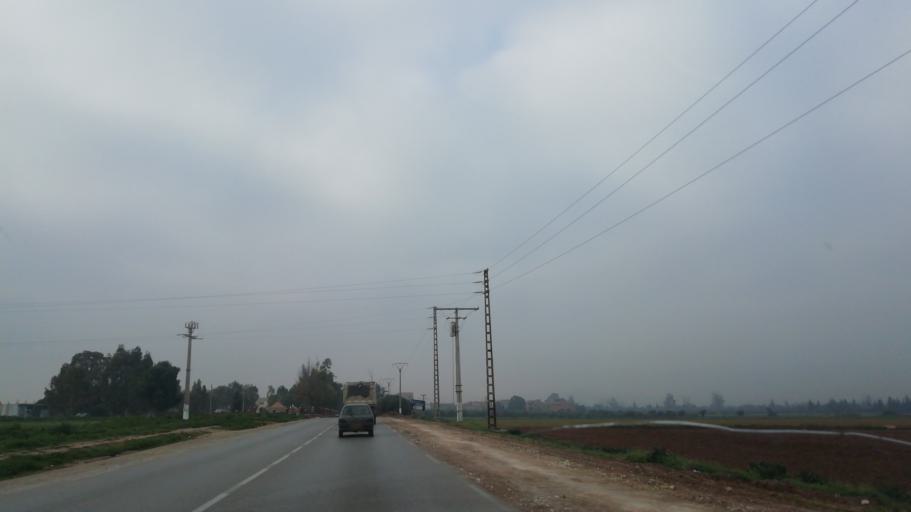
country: DZ
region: Relizane
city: Djidiouia
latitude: 35.9135
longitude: 0.7842
